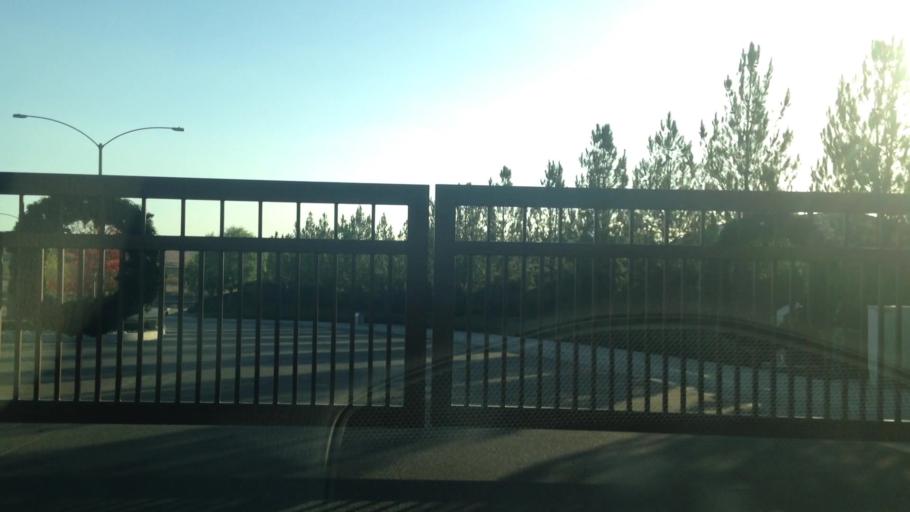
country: US
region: California
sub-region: Riverside County
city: Beaumont
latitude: 33.9454
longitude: -117.0229
